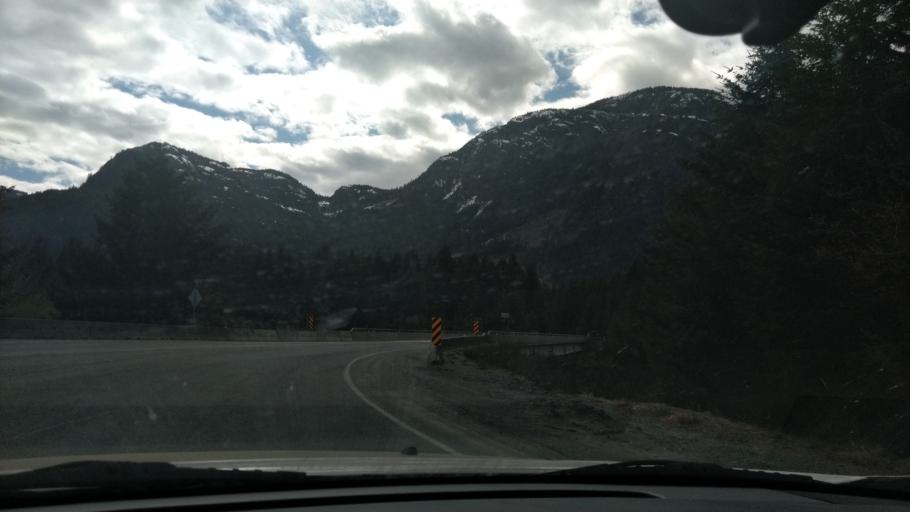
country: CA
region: British Columbia
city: Campbell River
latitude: 49.8371
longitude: -125.6333
